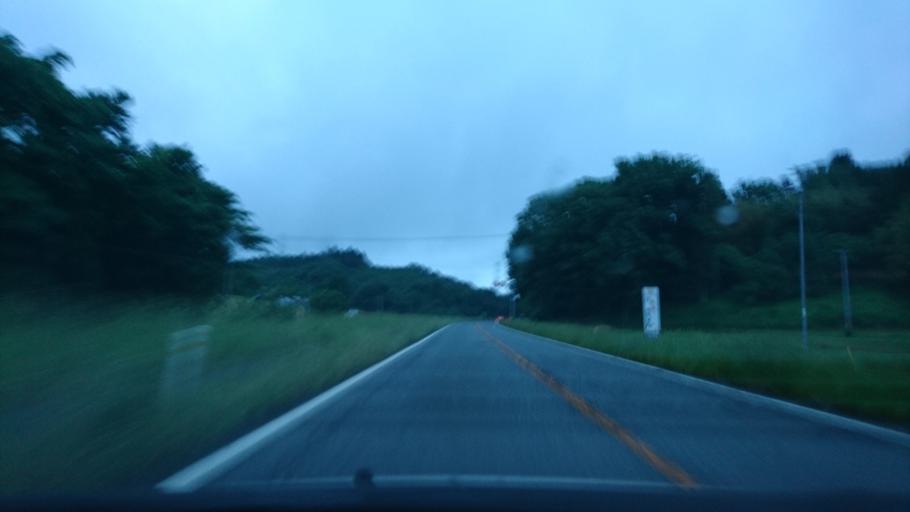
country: JP
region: Iwate
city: Ichinoseki
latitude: 38.8642
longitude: 141.1068
